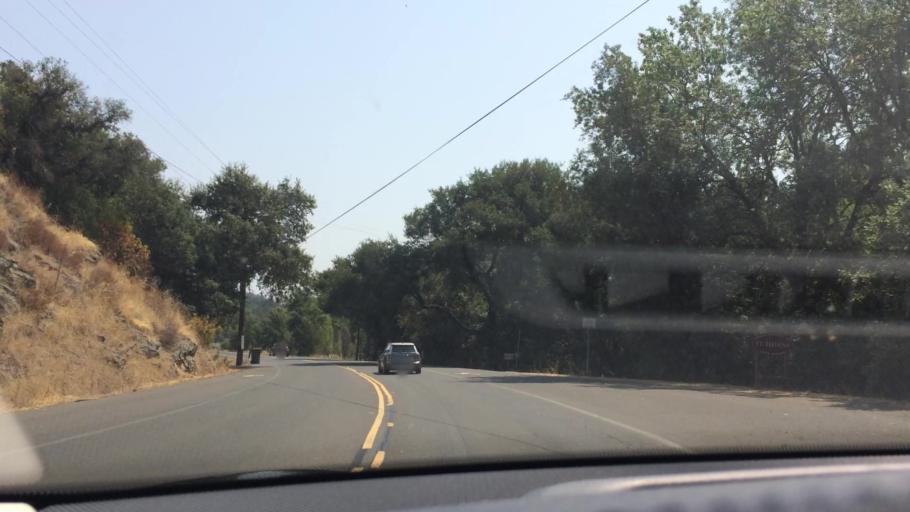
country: US
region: California
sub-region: Napa County
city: Deer Park
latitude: 38.5567
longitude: -122.5050
